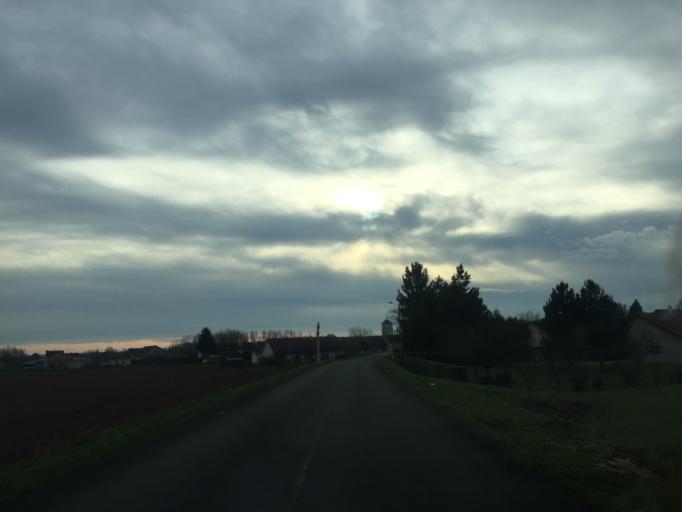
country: FR
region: Franche-Comte
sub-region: Departement du Jura
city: Tavaux
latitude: 47.0233
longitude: 5.4163
